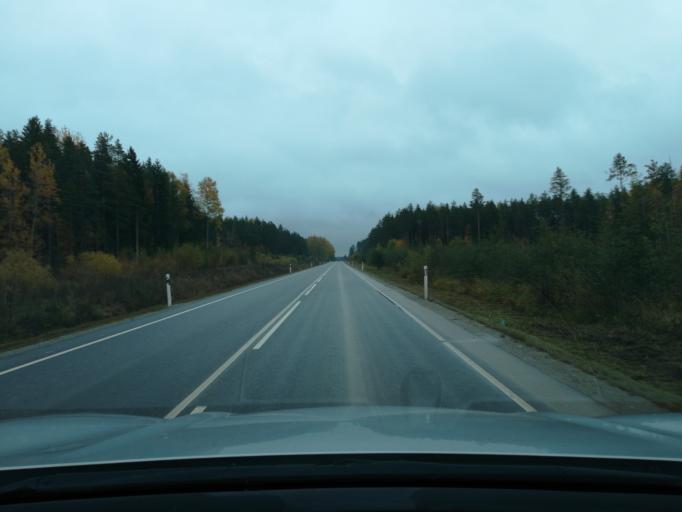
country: EE
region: Ida-Virumaa
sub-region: Johvi vald
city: Johvi
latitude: 59.2995
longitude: 27.4739
